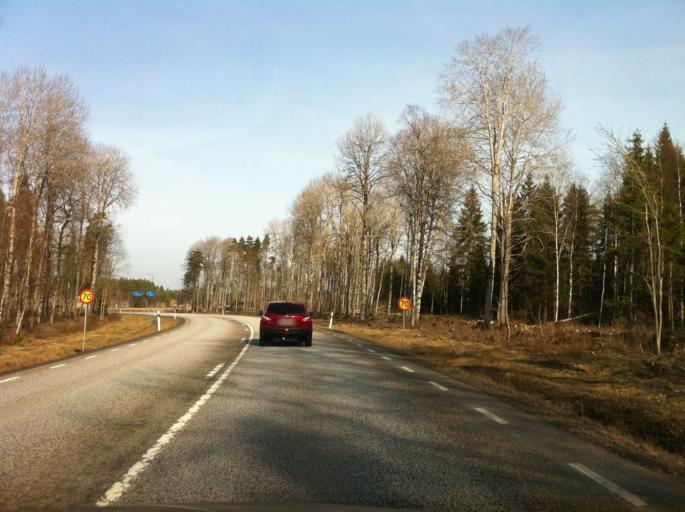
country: SE
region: Joenkoeping
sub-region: Mullsjo Kommun
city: Mullsjoe
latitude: 58.0302
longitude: 13.8374
